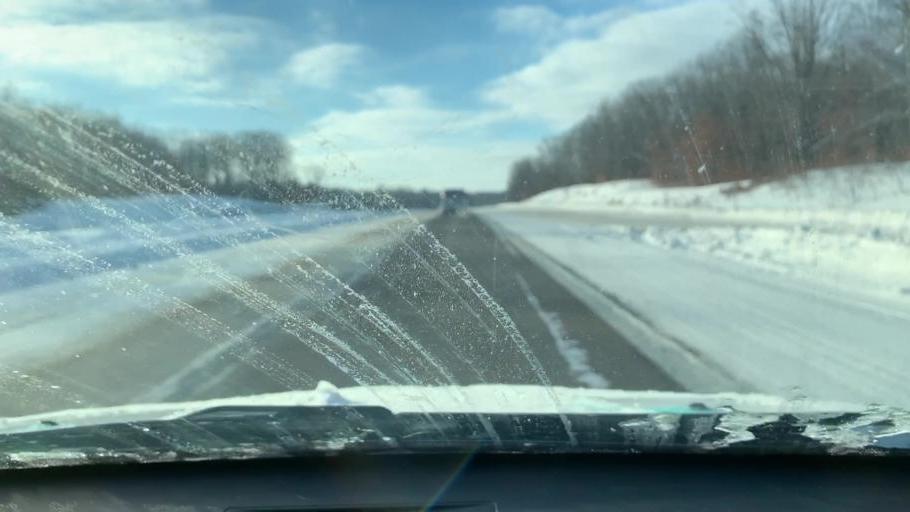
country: US
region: Michigan
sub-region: Wexford County
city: Cadillac
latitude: 44.2478
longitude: -85.3684
